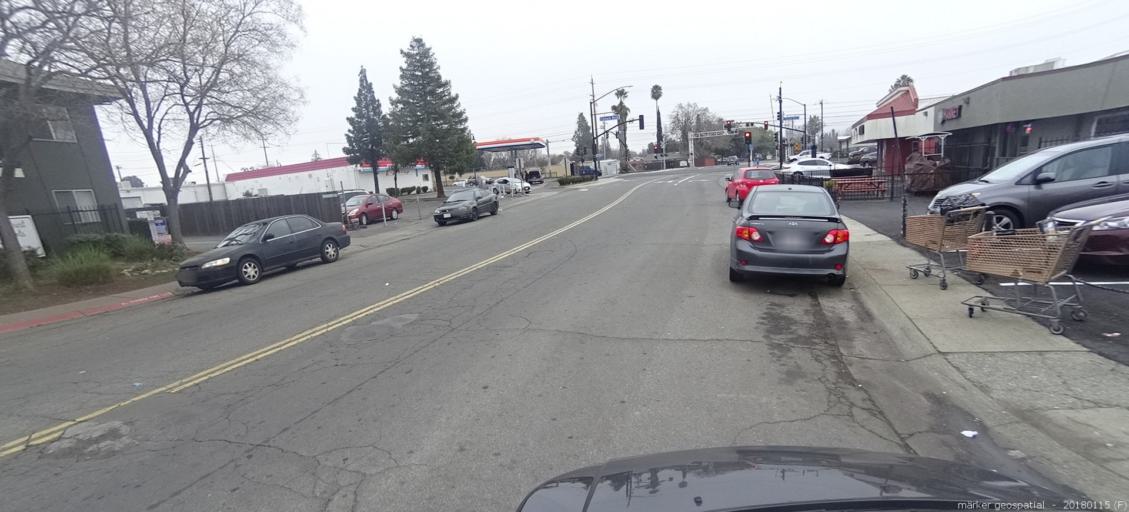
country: US
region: California
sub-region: Sacramento County
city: Rancho Cordova
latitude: 38.5927
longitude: -121.2974
